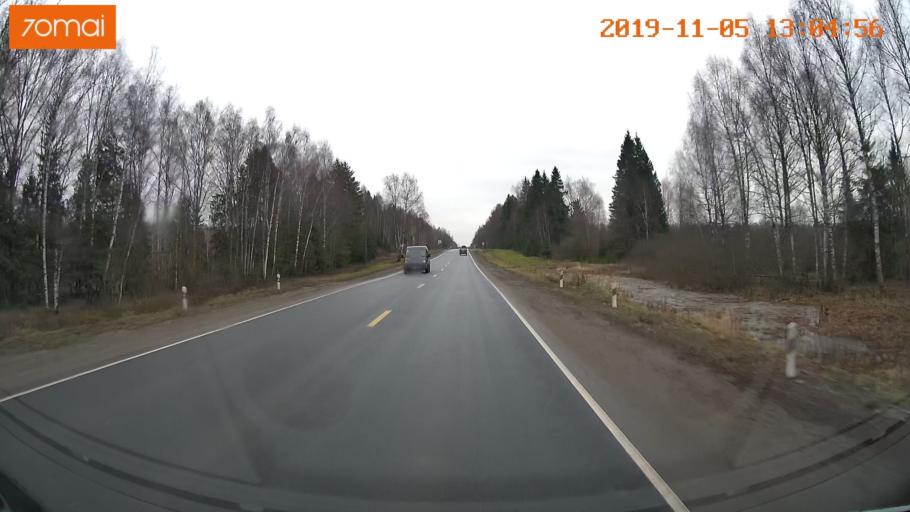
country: RU
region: Ivanovo
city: Kitovo
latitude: 56.8858
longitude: 41.2321
